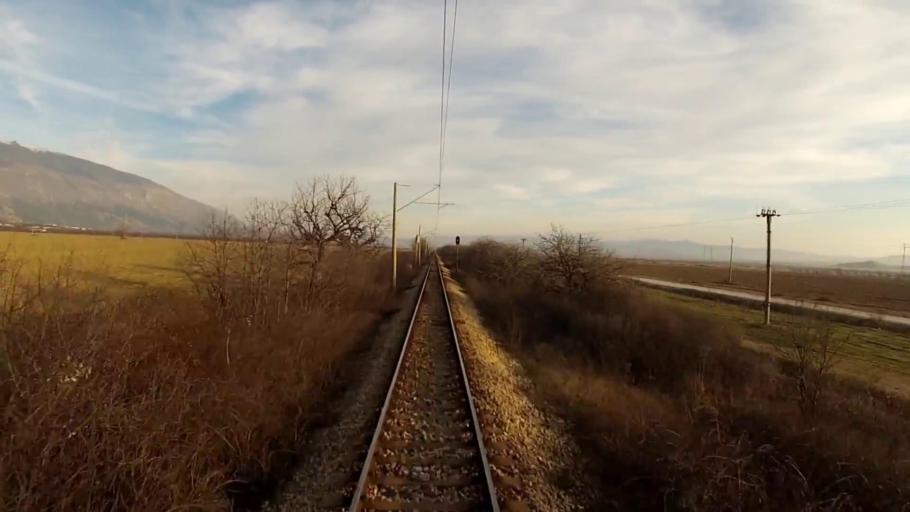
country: BG
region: Plovdiv
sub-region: Obshtina Karlovo
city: Karlovo
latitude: 42.6356
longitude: 24.7644
